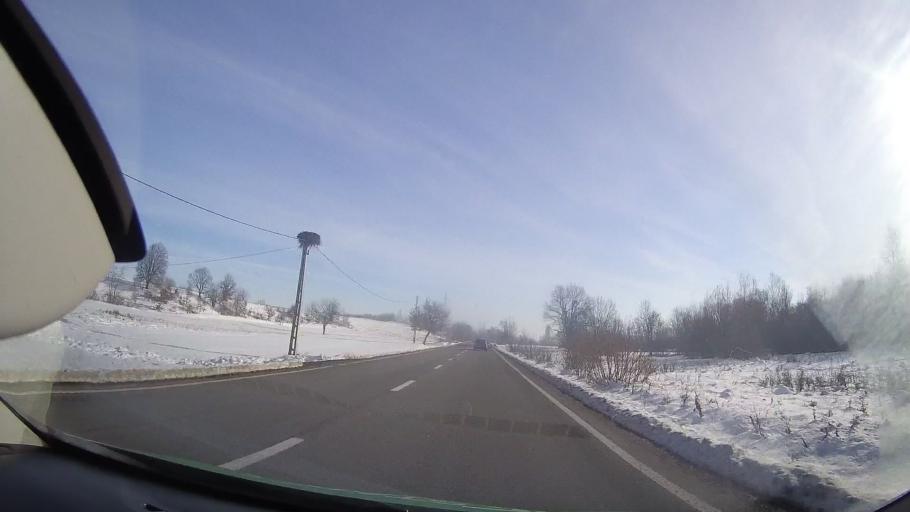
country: RO
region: Neamt
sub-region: Comuna Ghindaoani
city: Ghindaoani
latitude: 47.0753
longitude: 26.3550
